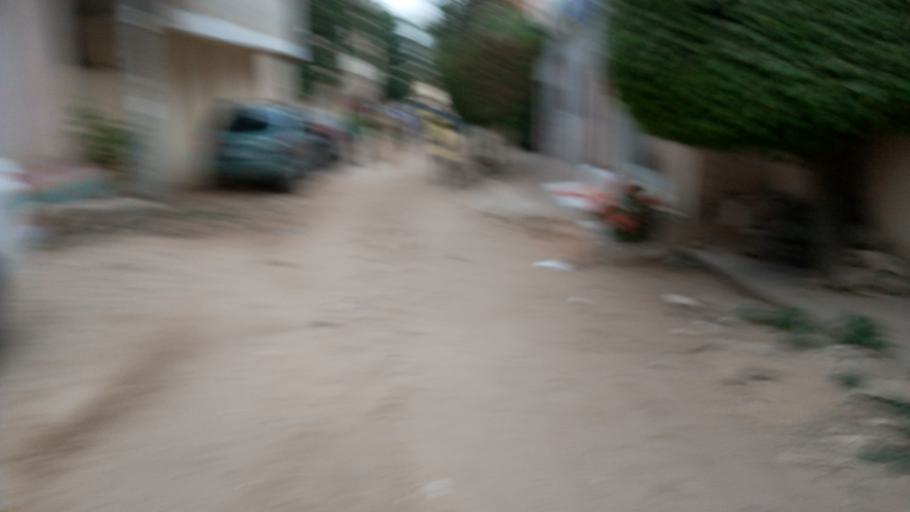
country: SN
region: Dakar
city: Grand Dakar
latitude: 14.7317
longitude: -17.4611
